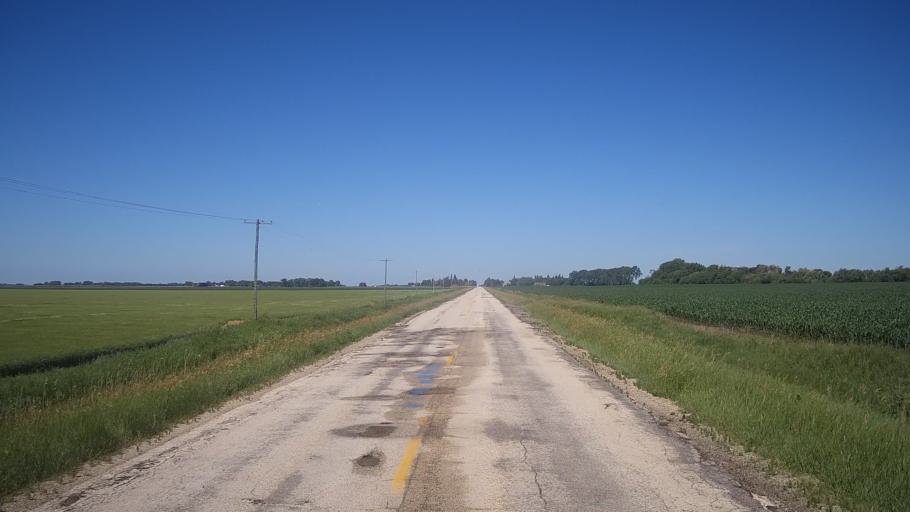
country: CA
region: Manitoba
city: Portage la Prairie
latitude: 50.0437
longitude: -98.0387
